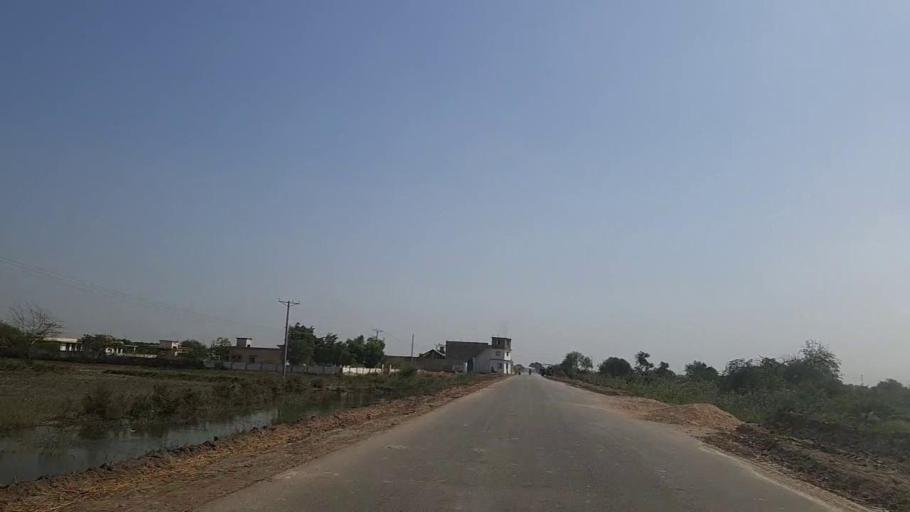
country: PK
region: Sindh
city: Daro Mehar
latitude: 24.7793
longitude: 68.2002
